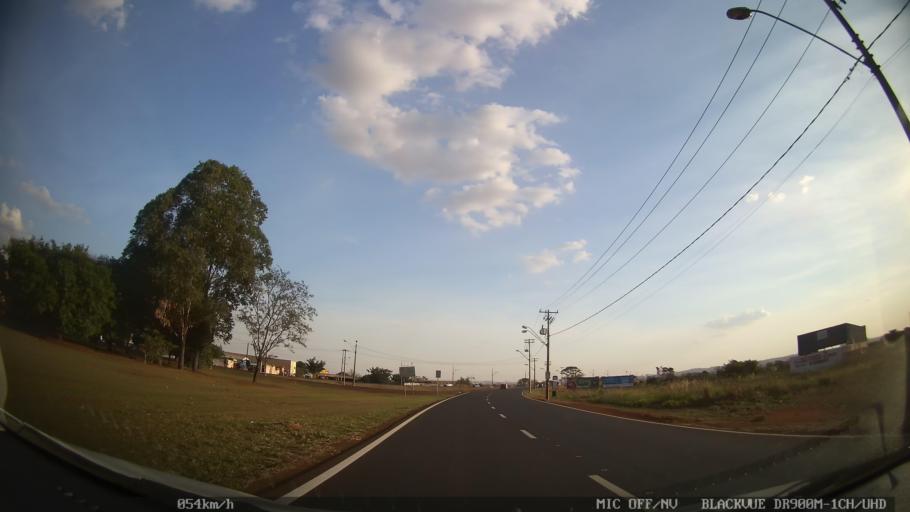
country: BR
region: Sao Paulo
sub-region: Ribeirao Preto
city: Ribeirao Preto
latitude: -21.1278
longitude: -47.7870
